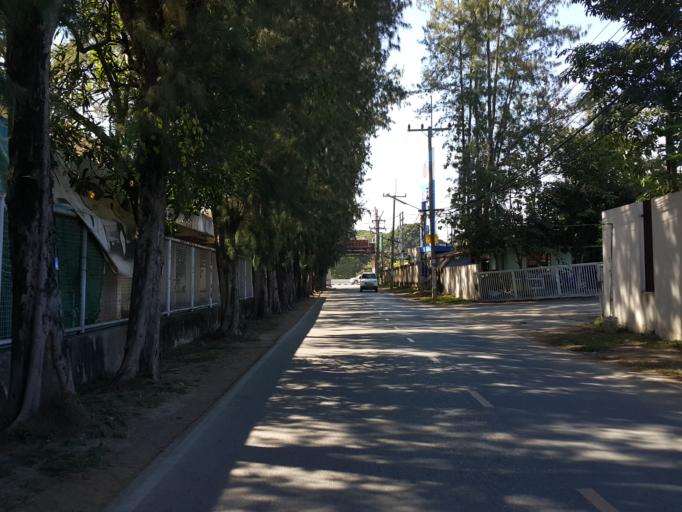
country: TH
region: Chiang Mai
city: Chiang Mai
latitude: 18.7788
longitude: 99.0289
